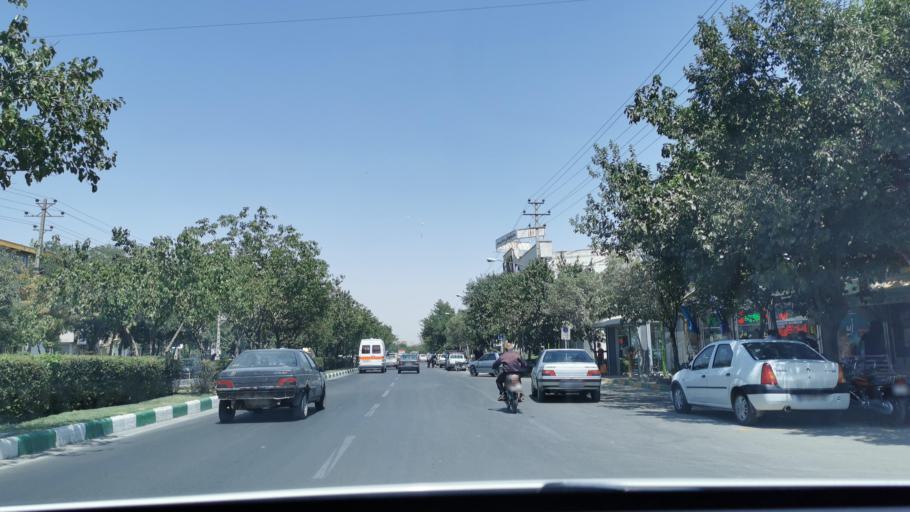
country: IR
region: Razavi Khorasan
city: Mashhad
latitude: 36.3439
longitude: 59.6260
